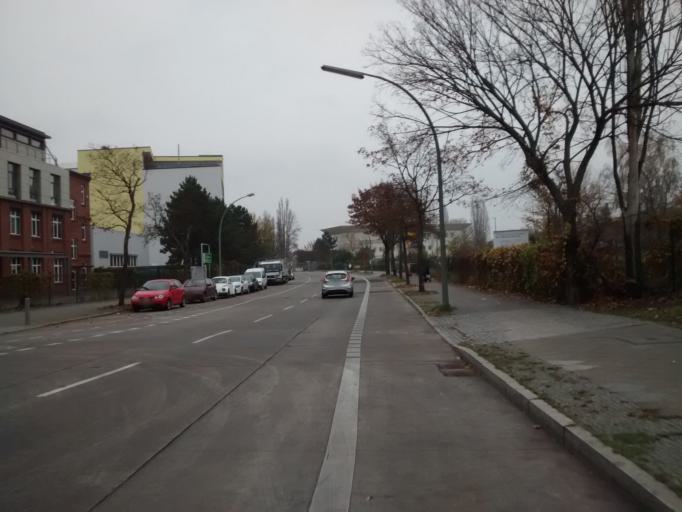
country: DE
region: Berlin
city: Charlottenburg-Nord
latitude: 52.5269
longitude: 13.3063
